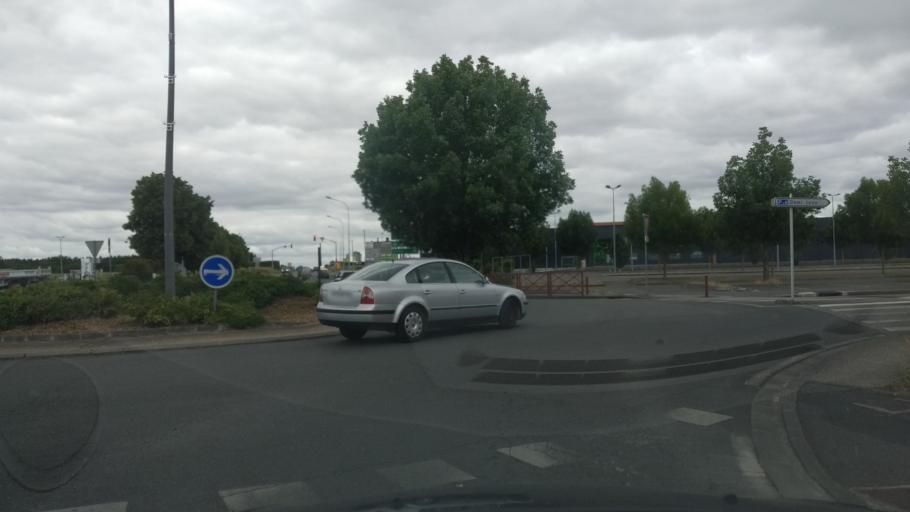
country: FR
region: Poitou-Charentes
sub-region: Departement de la Vienne
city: Poitiers
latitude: 46.5989
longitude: 0.3235
